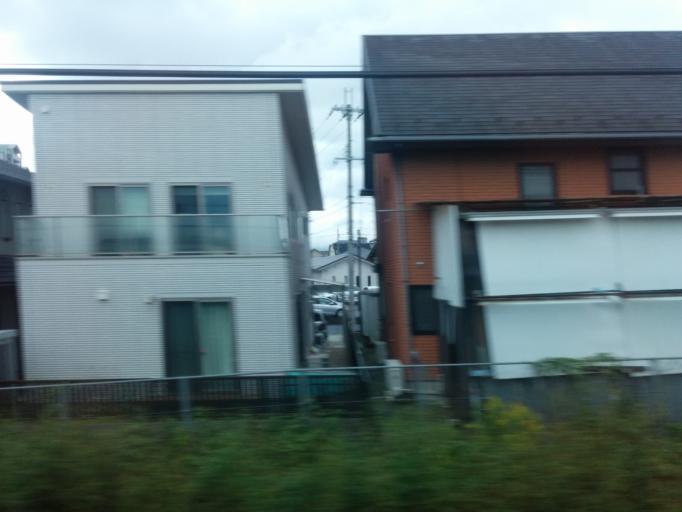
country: JP
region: Shiga Prefecture
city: Kusatsu
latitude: 35.0359
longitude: 135.9781
